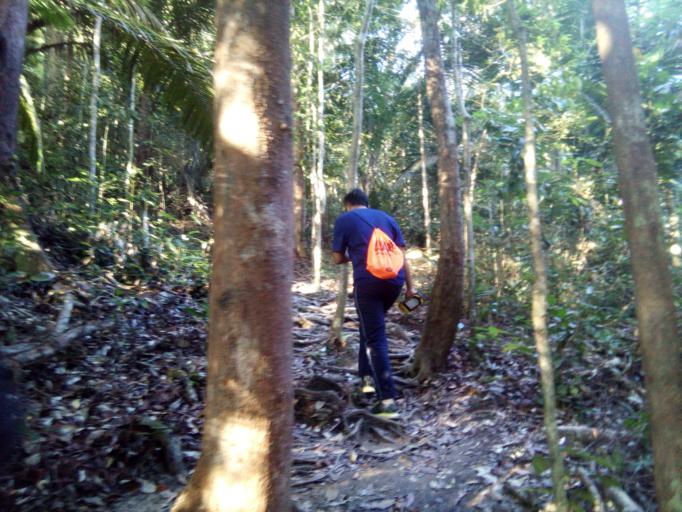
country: MY
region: Penang
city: Tanjung Tokong
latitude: 5.4320
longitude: 100.2880
